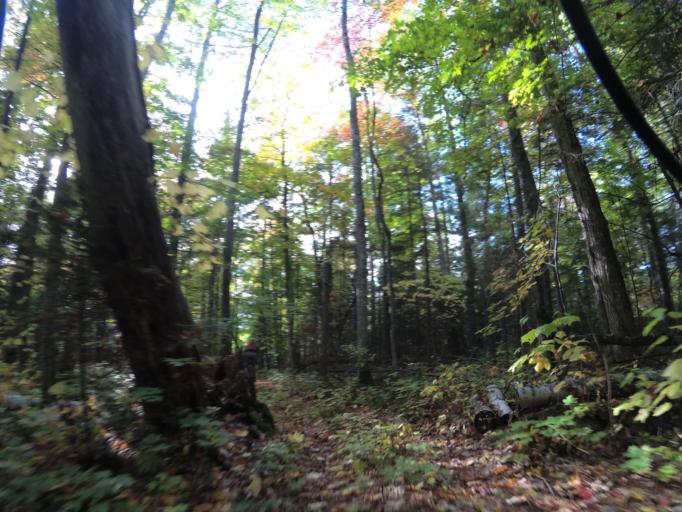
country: CA
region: Ontario
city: Pembroke
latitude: 45.3303
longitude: -77.1804
